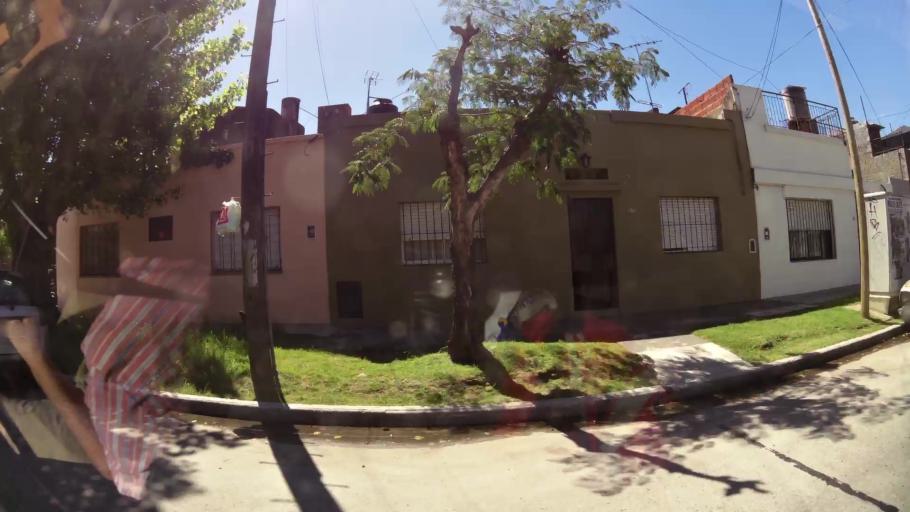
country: AR
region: Buenos Aires
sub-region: Partido de General San Martin
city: General San Martin
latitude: -34.5301
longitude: -58.5558
